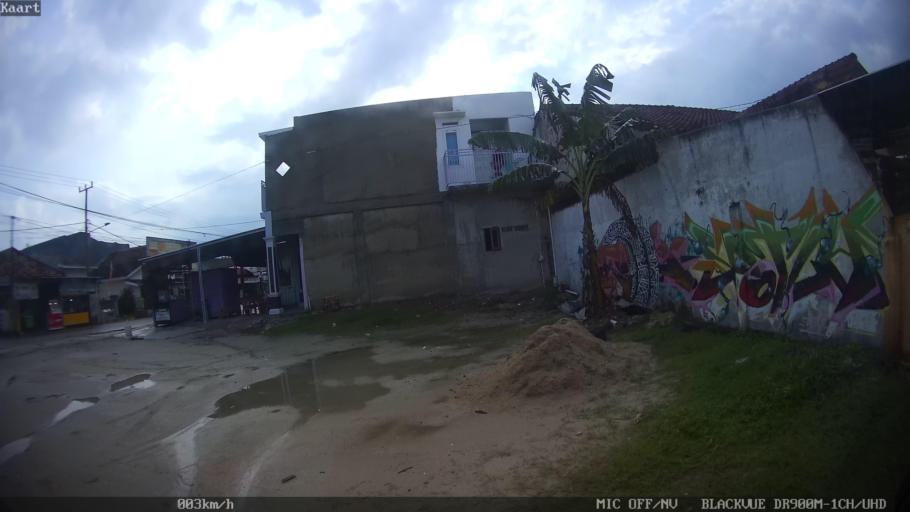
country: ID
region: Lampung
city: Kedaton
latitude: -5.3910
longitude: 105.2966
